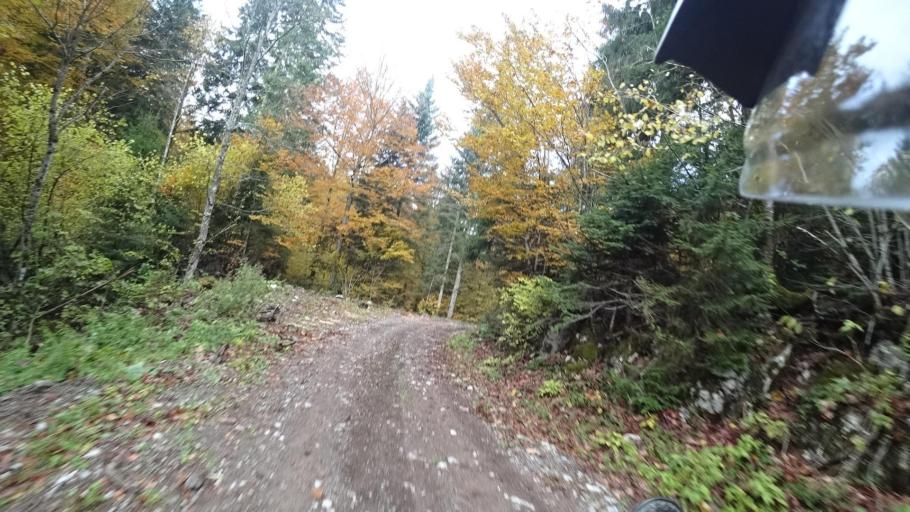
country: HR
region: Primorsko-Goranska
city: Vrbovsko
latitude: 45.2128
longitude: 15.0731
